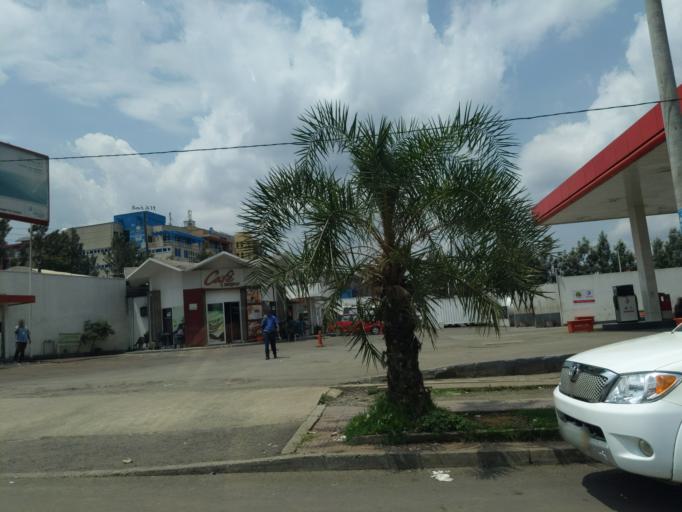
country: ET
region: Adis Abeba
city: Addis Ababa
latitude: 8.9596
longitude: 38.7640
